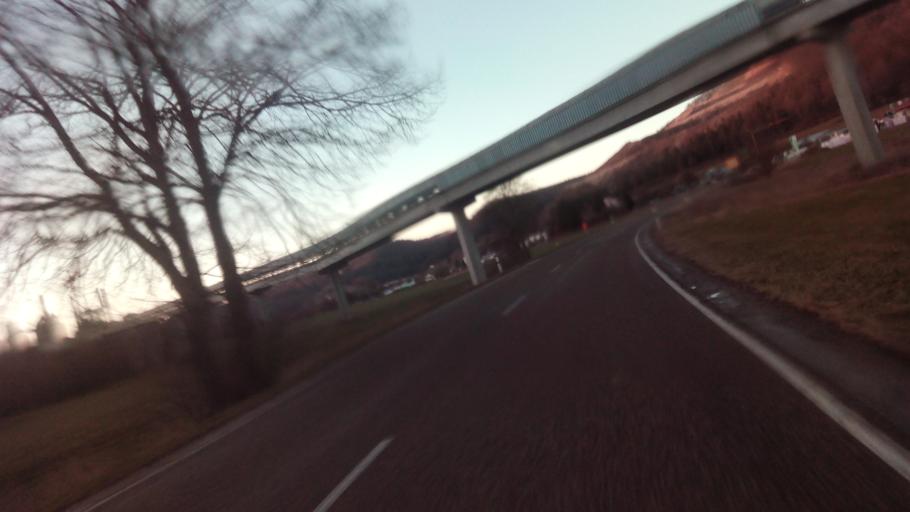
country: DE
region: Baden-Wuerttemberg
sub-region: Tuebingen Region
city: Schelklingen
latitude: 48.3638
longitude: 9.7434
